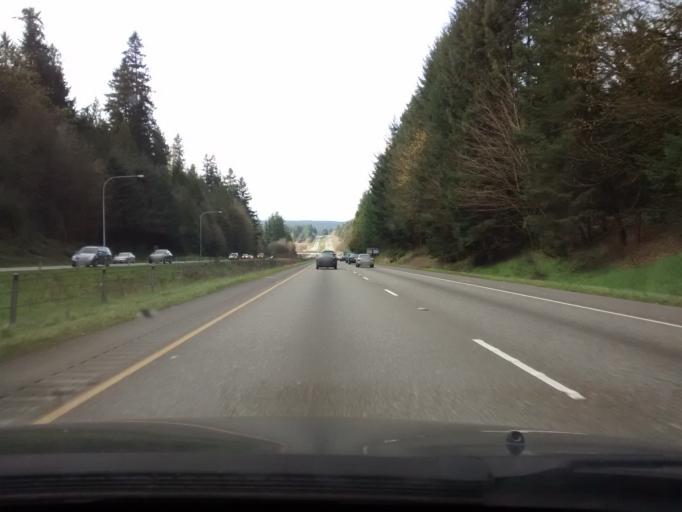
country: US
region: Washington
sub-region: Pierce County
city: Canterwood
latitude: 47.3515
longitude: -122.6113
